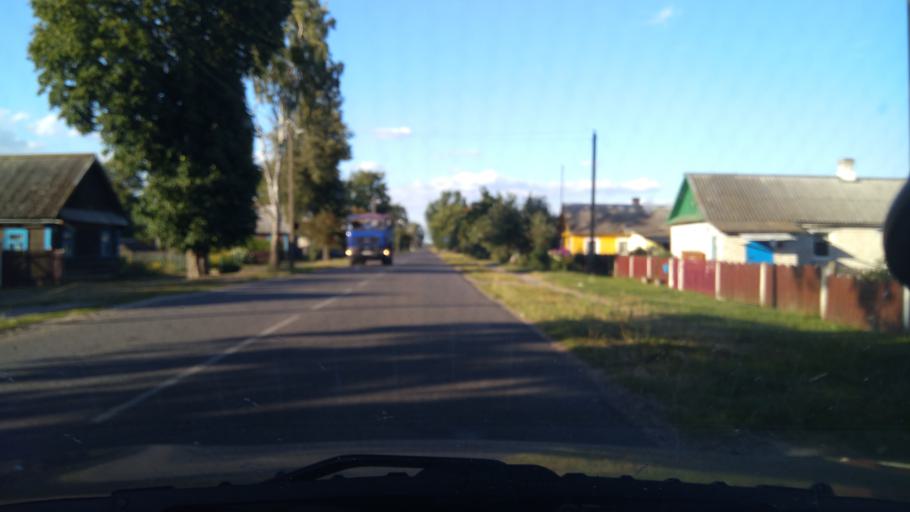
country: BY
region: Brest
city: Byaroza
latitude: 52.5842
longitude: 24.8639
